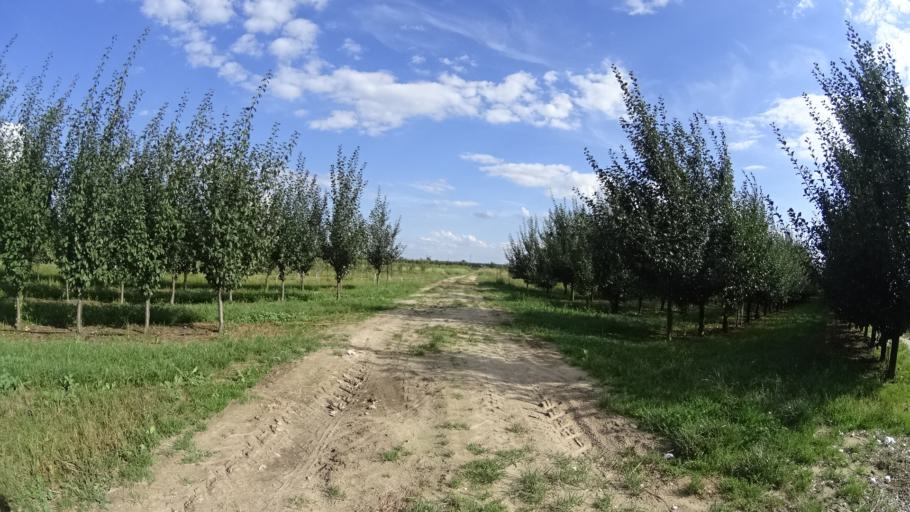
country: PL
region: Masovian Voivodeship
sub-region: Powiat bialobrzeski
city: Wysmierzyce
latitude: 51.6656
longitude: 20.8126
